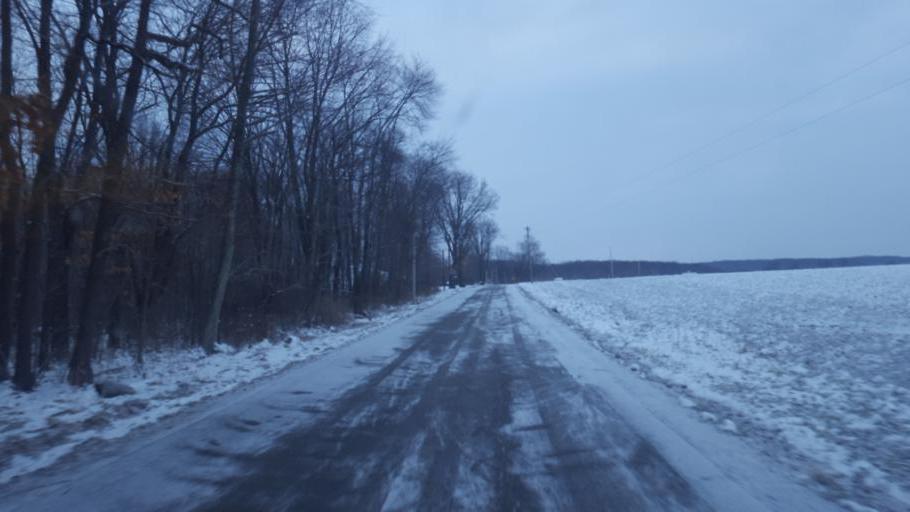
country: US
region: Pennsylvania
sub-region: Venango County
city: Sugarcreek
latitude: 41.4339
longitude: -79.9799
